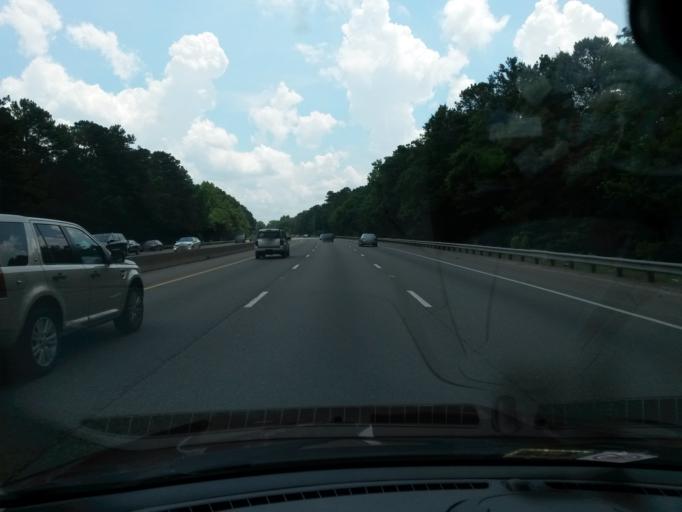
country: US
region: Virginia
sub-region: Chesterfield County
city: Bellwood
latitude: 37.3898
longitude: -77.4216
